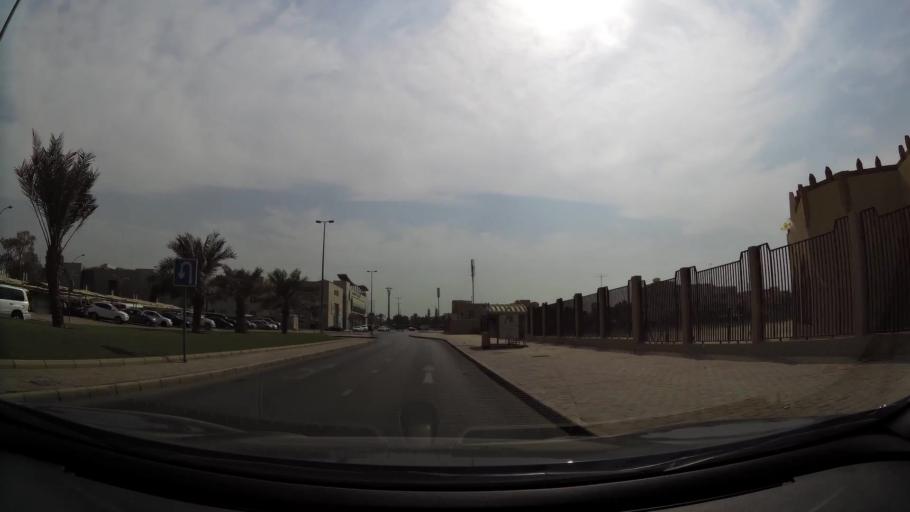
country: KW
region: Al Asimah
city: Ash Shamiyah
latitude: 29.3408
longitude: 47.9616
